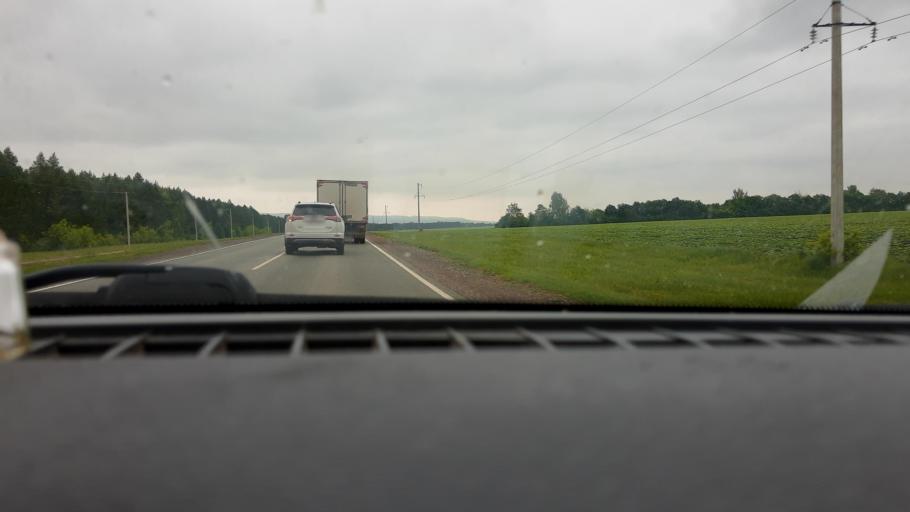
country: RU
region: Bashkortostan
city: Serafimovskiy
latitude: 54.4348
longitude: 53.9760
